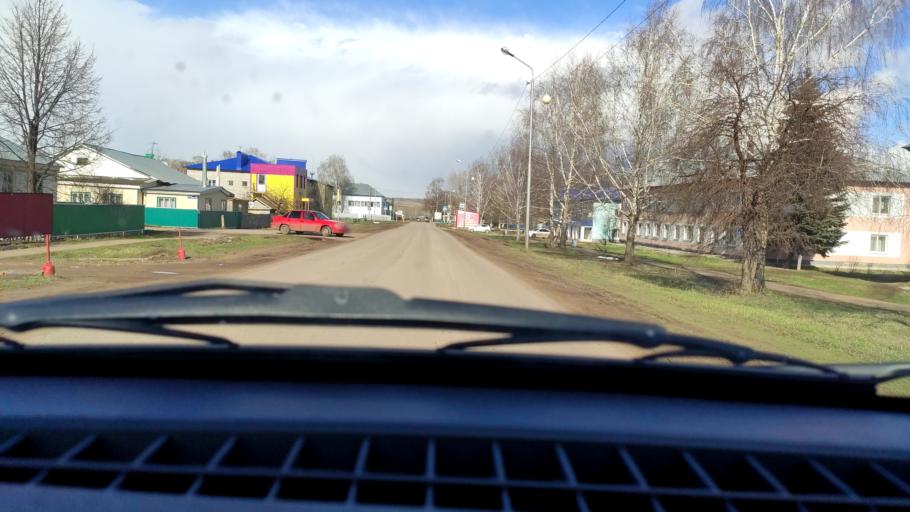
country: RU
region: Bashkortostan
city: Chekmagush
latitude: 55.1427
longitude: 54.6461
